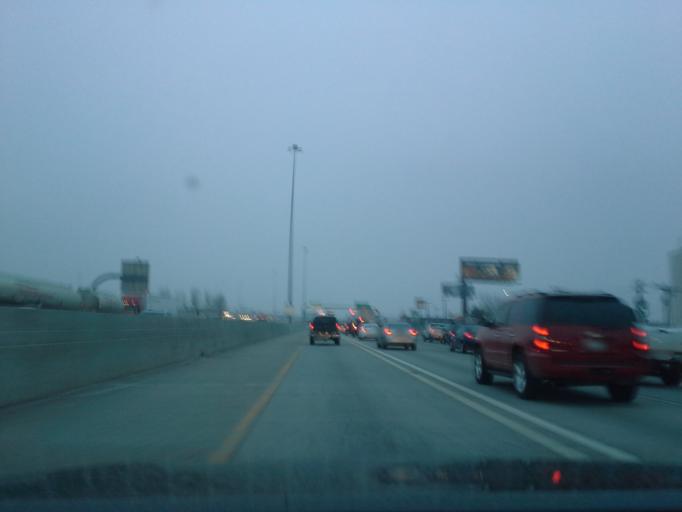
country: US
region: Utah
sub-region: Salt Lake County
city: Centerfield
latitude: 40.7072
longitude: -111.9038
